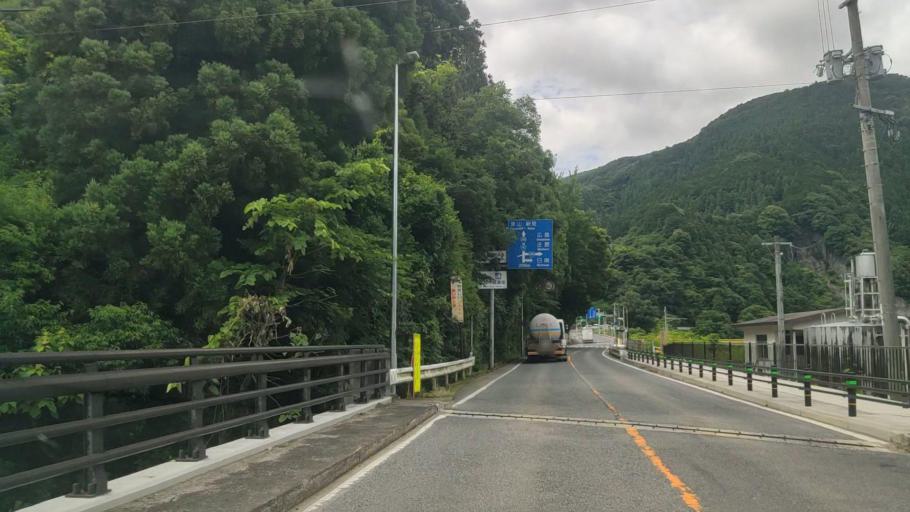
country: JP
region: Tottori
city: Yonago
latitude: 35.2382
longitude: 133.4399
